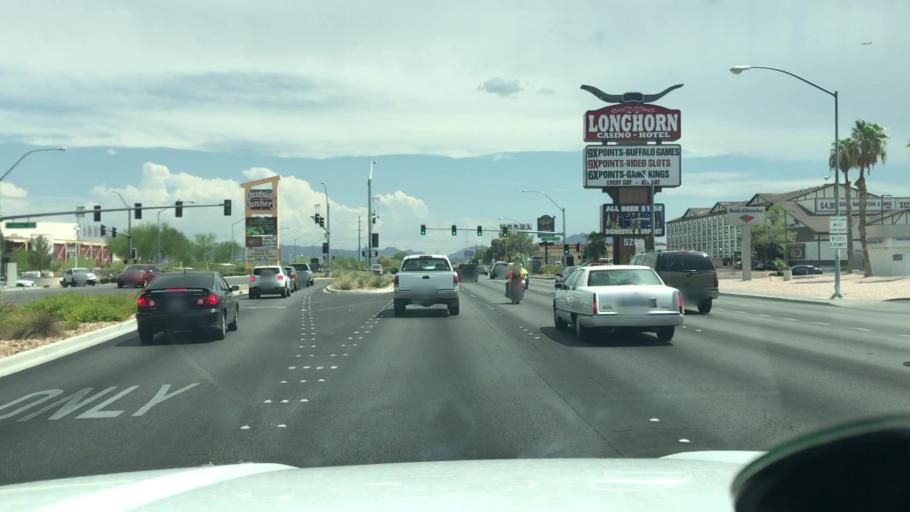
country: US
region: Nevada
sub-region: Clark County
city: Whitney
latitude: 36.1087
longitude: -115.0599
